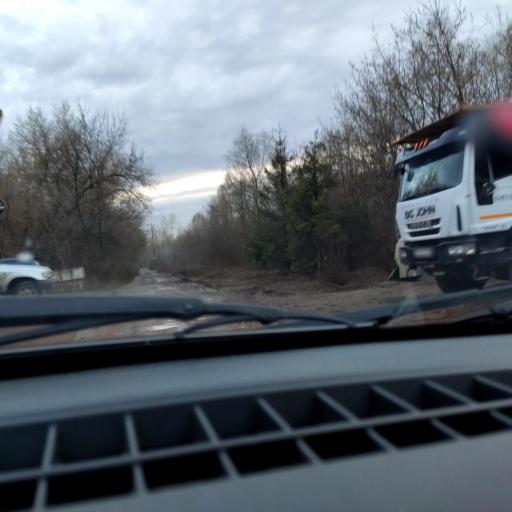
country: RU
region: Bashkortostan
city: Ufa
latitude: 54.6834
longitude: 55.9535
